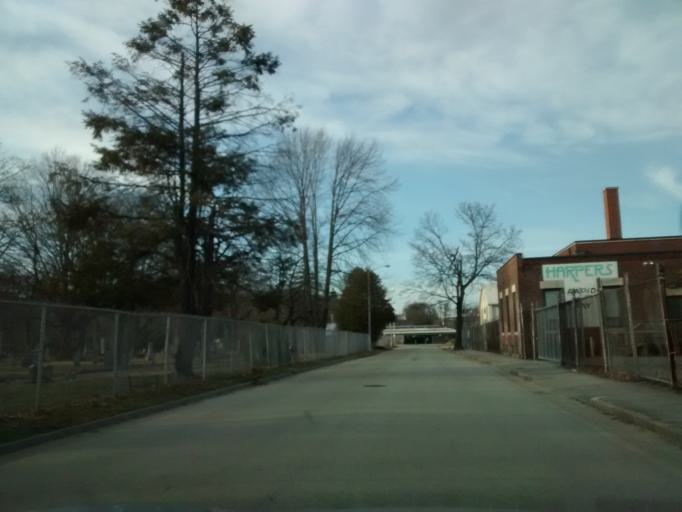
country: US
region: Massachusetts
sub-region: Worcester County
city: Worcester
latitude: 42.2802
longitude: -71.7996
